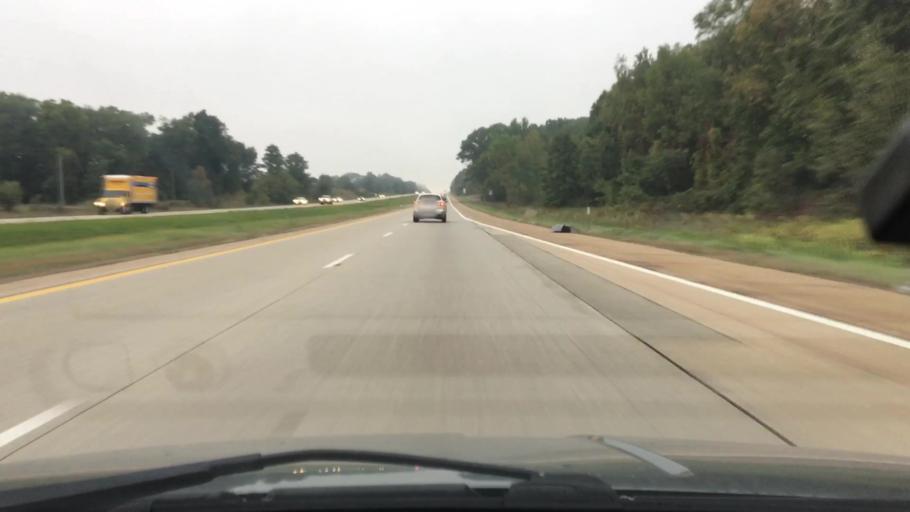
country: US
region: Michigan
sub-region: Jackson County
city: Concord
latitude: 42.2623
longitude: -84.6556
